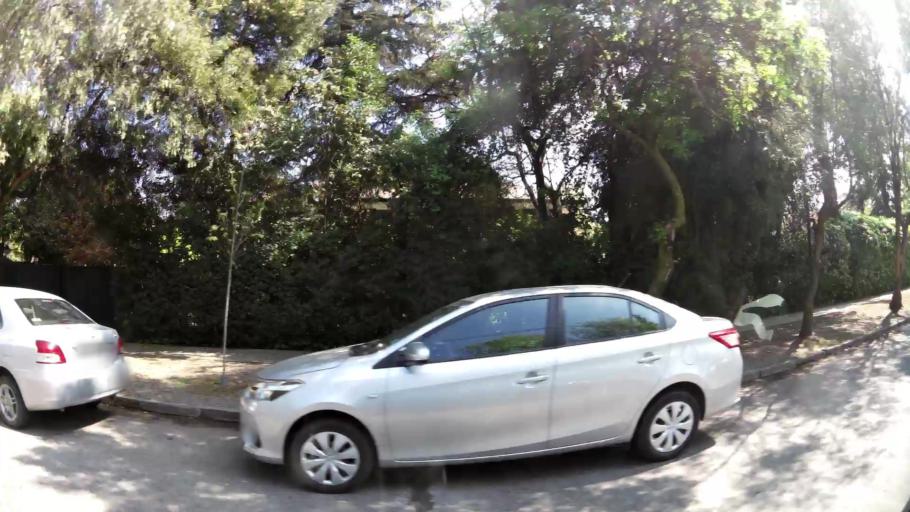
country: CL
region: Santiago Metropolitan
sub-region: Provincia de Santiago
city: Villa Presidente Frei, Nunoa, Santiago, Chile
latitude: -33.3902
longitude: -70.5821
